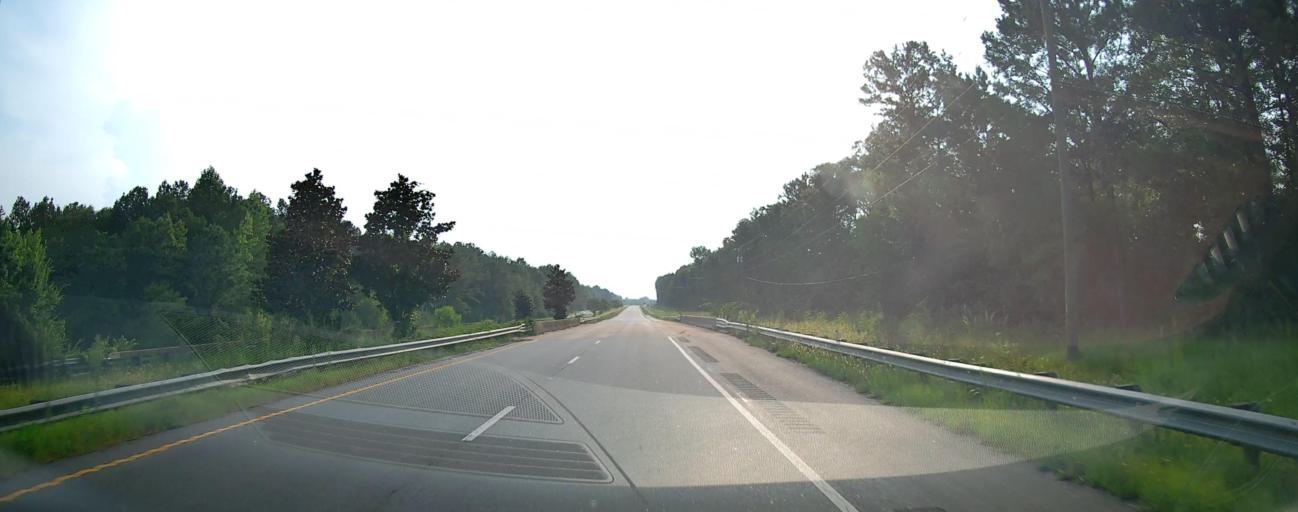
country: US
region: Georgia
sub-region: Talbot County
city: Talbotton
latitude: 32.5459
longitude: -84.7139
